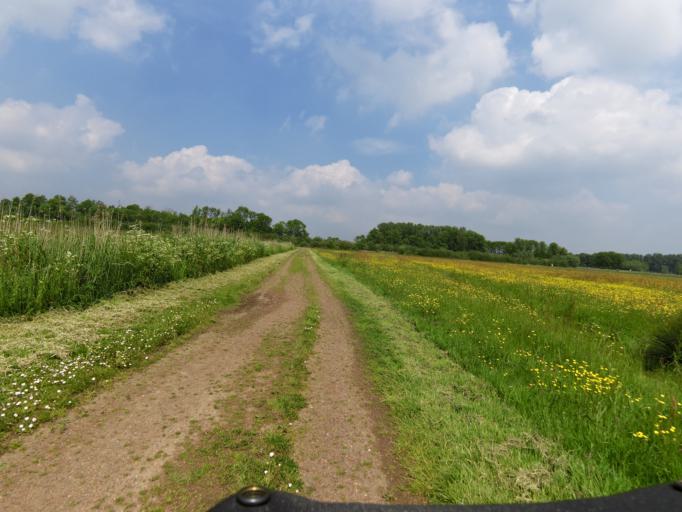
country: NL
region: South Holland
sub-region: Gemeente Spijkenisse
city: Spijkenisse
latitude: 51.8170
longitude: 4.2829
